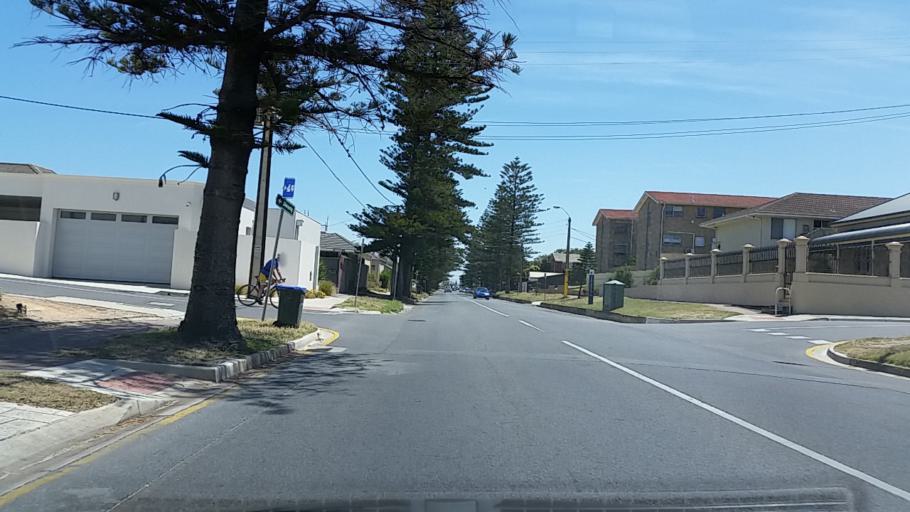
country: AU
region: South Australia
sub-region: Charles Sturt
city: Henley Beach
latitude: -34.9289
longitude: 138.4970
